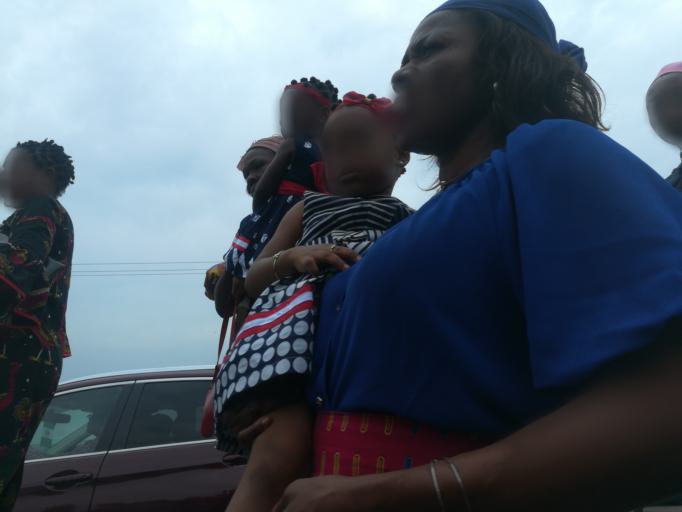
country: NG
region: Rivers
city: Port Harcourt
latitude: 4.8414
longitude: 6.9847
